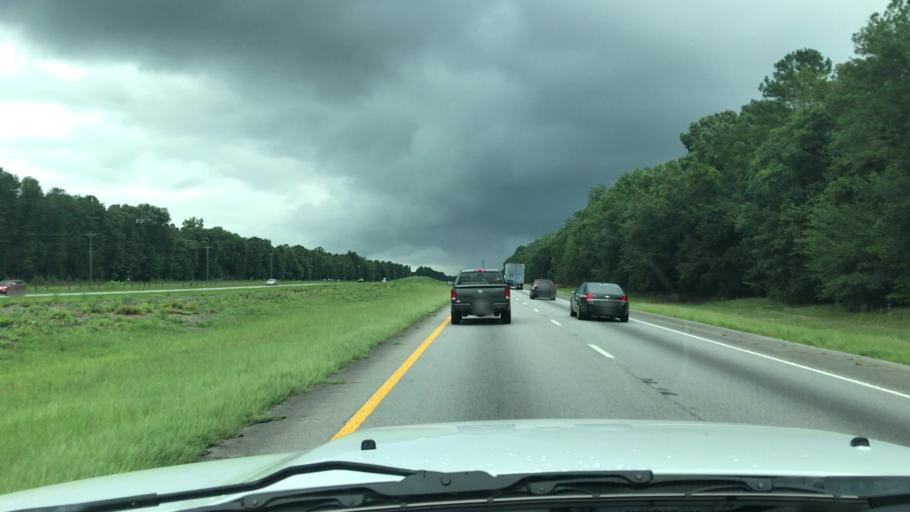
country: US
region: South Carolina
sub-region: Jasper County
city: Ridgeland
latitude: 32.5530
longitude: -80.9469
